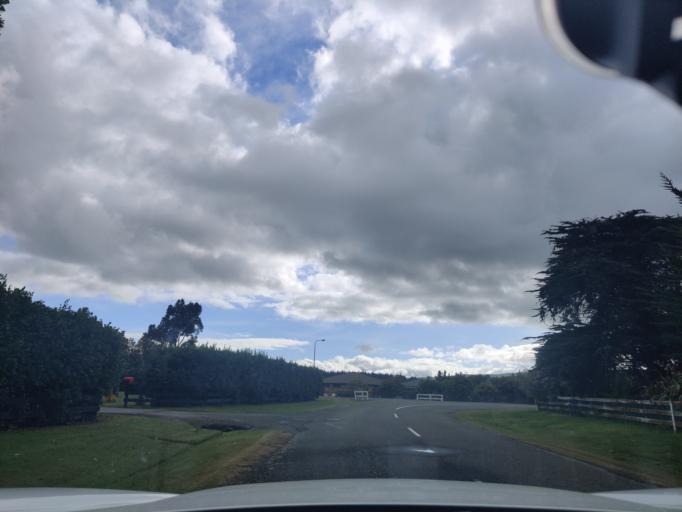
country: NZ
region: Manawatu-Wanganui
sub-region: Palmerston North City
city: Palmerston North
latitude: -40.3767
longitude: 175.6597
